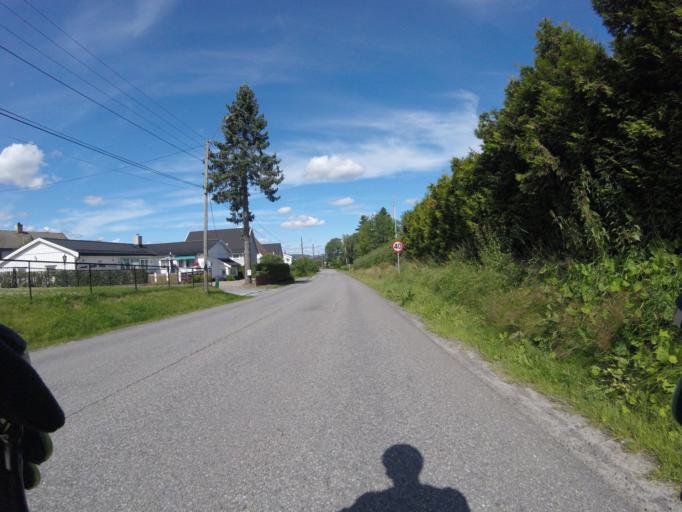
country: NO
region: Akershus
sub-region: Skedsmo
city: Lillestrom
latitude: 59.9488
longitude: 11.0208
